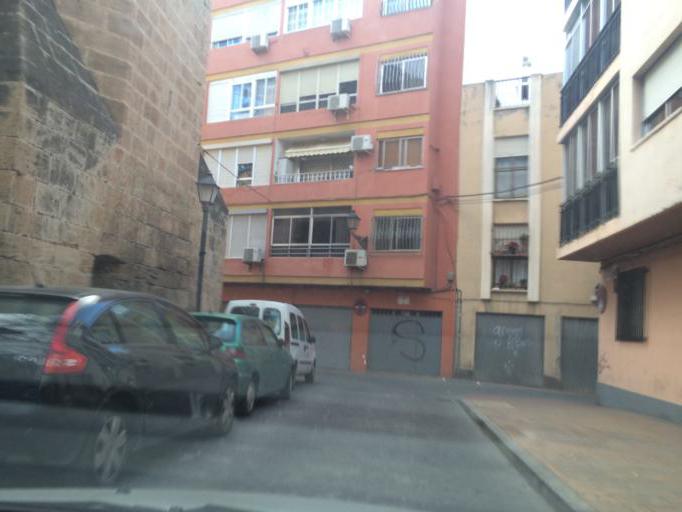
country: ES
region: Andalusia
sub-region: Provincia de Almeria
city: Almeria
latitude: 36.8380
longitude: -2.4680
